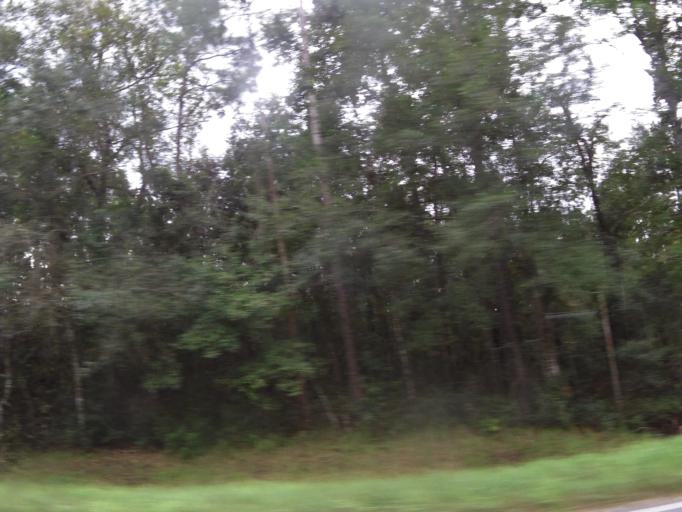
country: US
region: Florida
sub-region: Clay County
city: Middleburg
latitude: 30.1140
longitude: -81.8632
